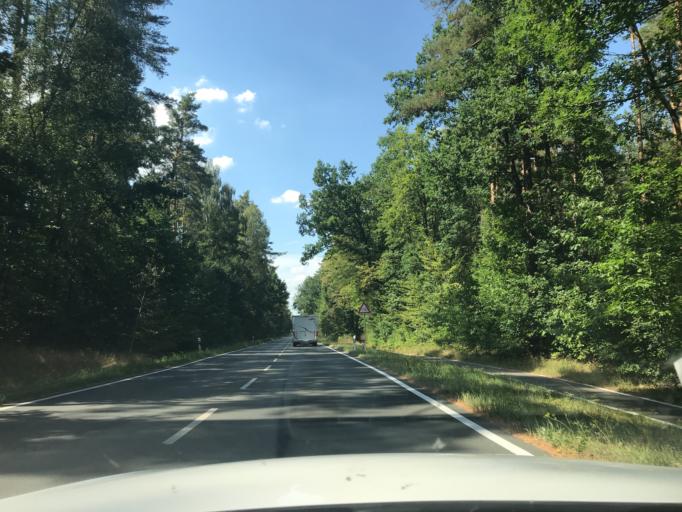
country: DE
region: Bavaria
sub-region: Regierungsbezirk Mittelfranken
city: Erlangen
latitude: 49.5596
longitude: 11.0140
